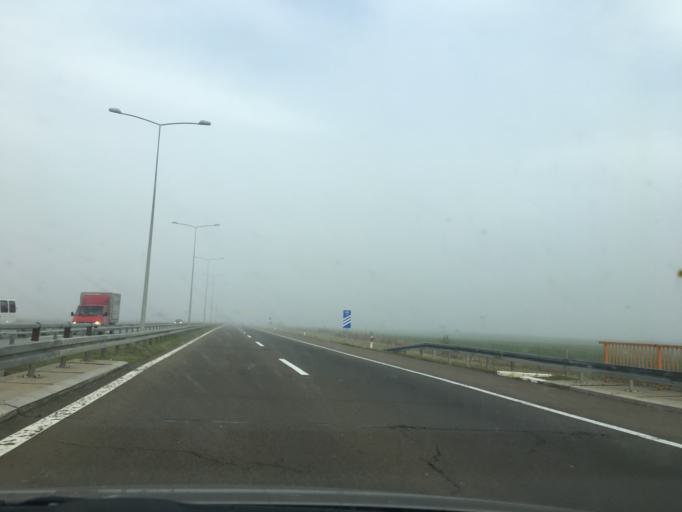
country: RS
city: Krcedin
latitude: 45.0952
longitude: 20.1195
